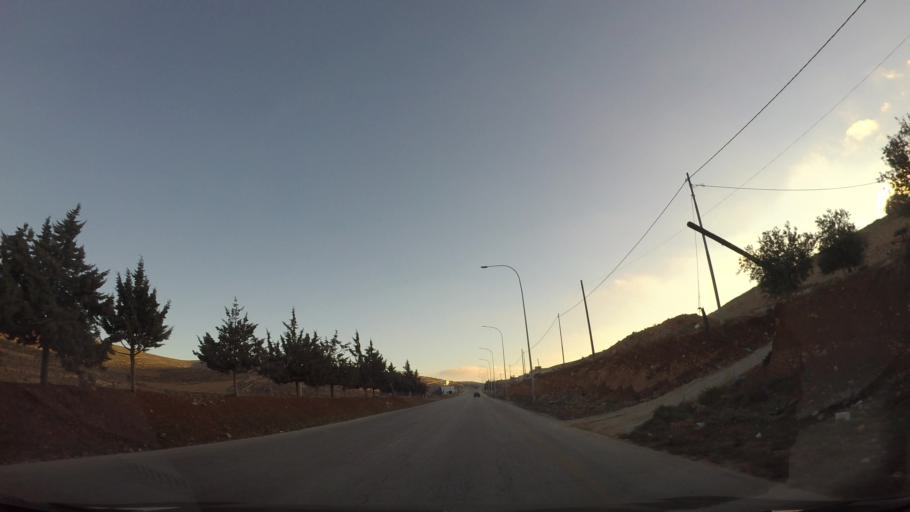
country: JO
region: Ma'an
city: Petra
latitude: 30.4259
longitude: 35.5138
